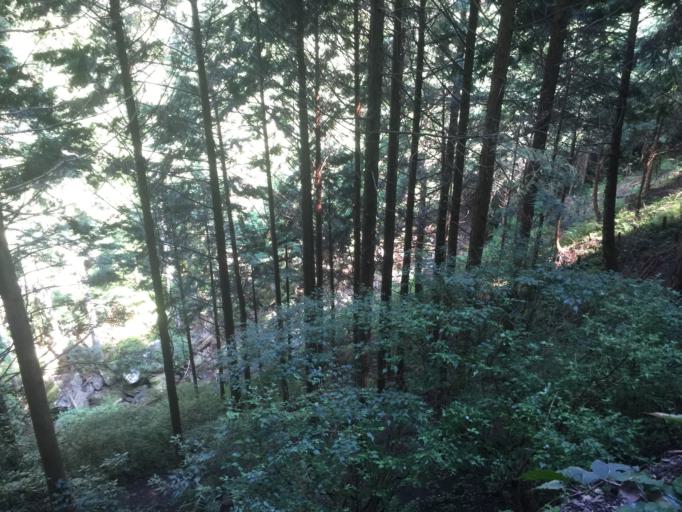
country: JP
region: Shizuoka
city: Kanaya
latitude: 34.8448
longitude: 138.0610
